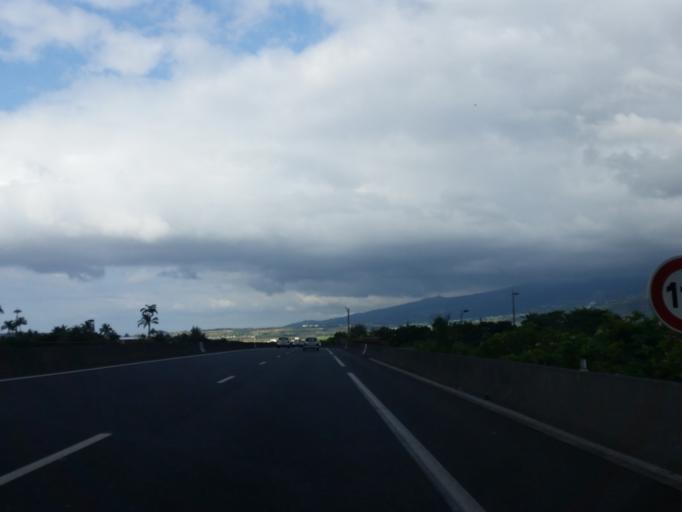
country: RE
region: Reunion
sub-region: Reunion
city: Saint-Paul
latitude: -21.0103
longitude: 55.2762
